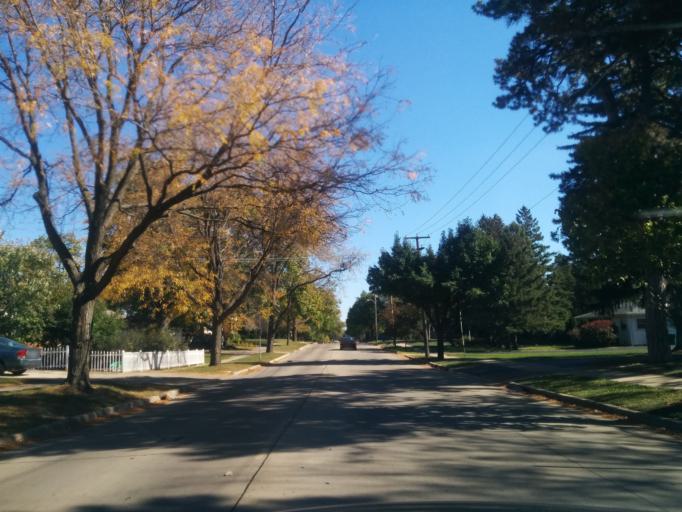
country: US
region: Illinois
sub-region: DuPage County
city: Lombard
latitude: 41.8748
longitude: -88.0122
